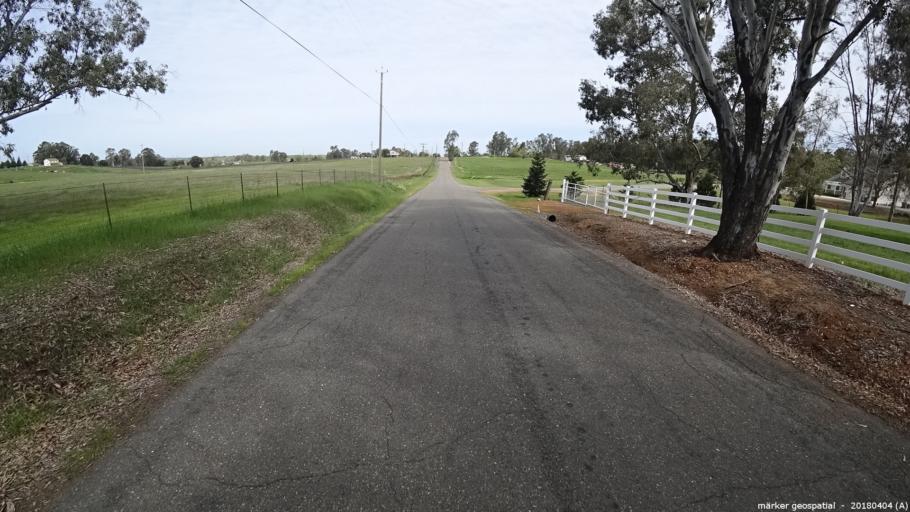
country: US
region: California
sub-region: Sacramento County
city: Clay
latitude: 38.3276
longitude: -121.1499
